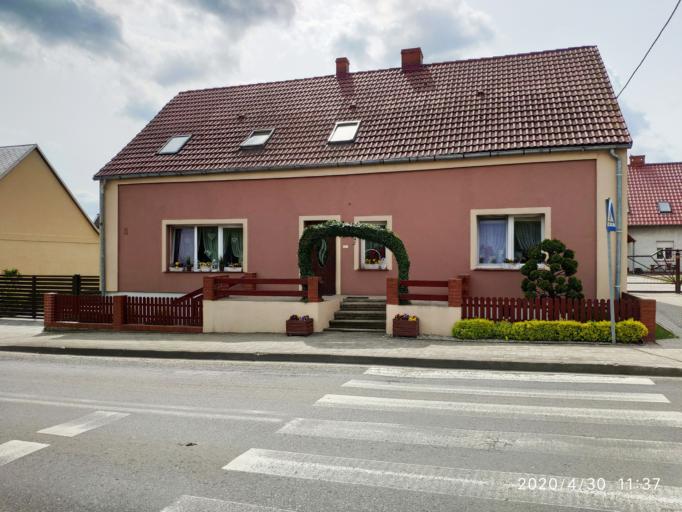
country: PL
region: Lubusz
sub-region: Powiat zielonogorski
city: Trzebiechow
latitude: 52.0435
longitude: 15.6943
